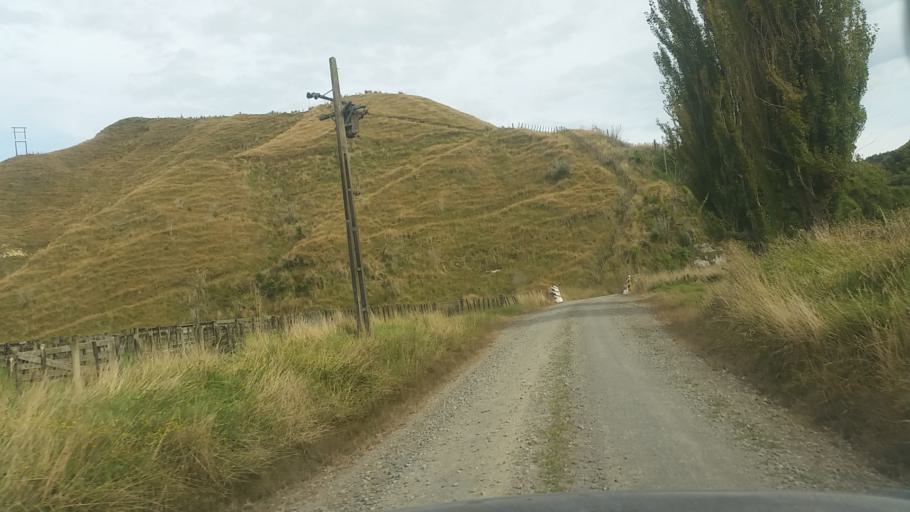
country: NZ
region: Taranaki
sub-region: New Plymouth District
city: Waitara
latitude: -39.1327
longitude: 174.7029
